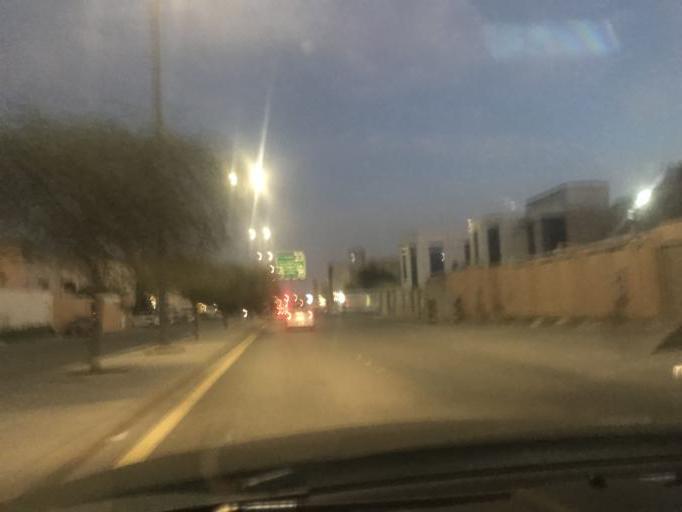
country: SA
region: Ar Riyad
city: Riyadh
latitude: 24.7333
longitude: 46.7604
